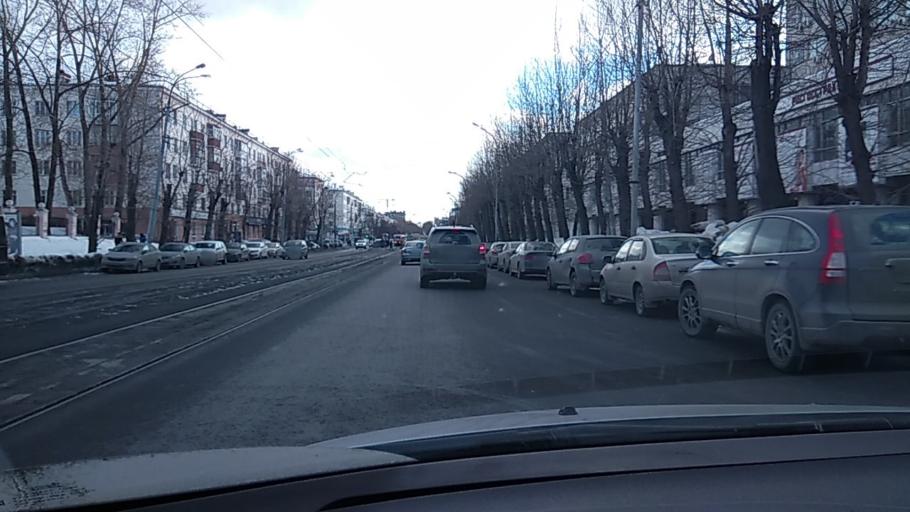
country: RU
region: Sverdlovsk
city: Yekaterinburg
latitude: 56.8450
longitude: 60.6446
